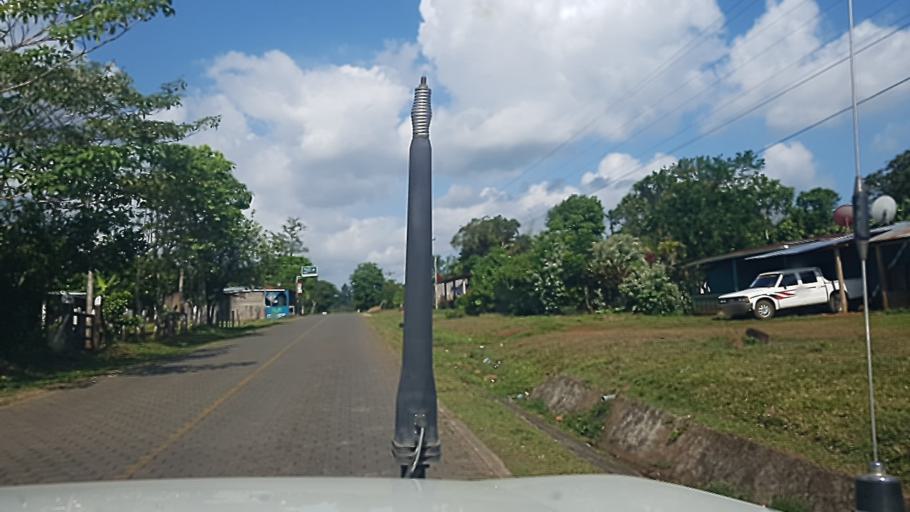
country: NI
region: Atlantico Sur
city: Nueva Guinea
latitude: 11.7017
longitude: -84.3787
